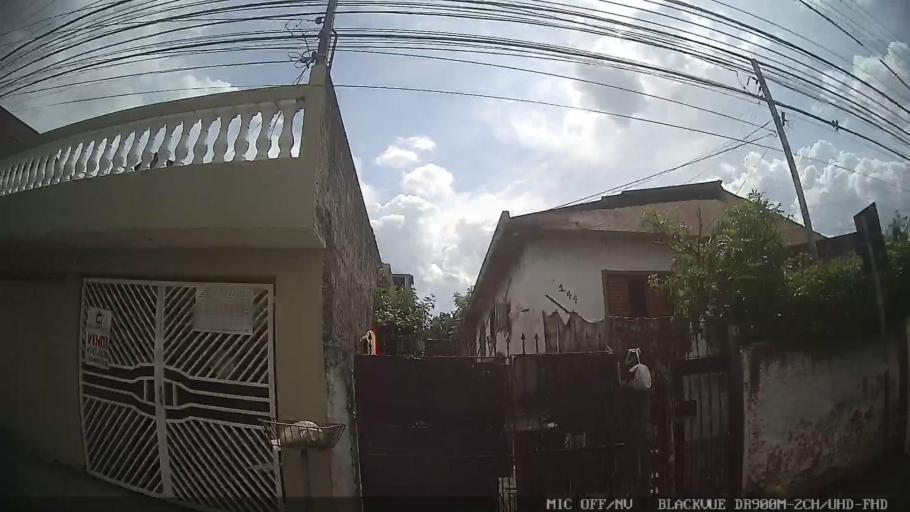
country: BR
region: Sao Paulo
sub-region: Poa
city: Poa
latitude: -23.5258
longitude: -46.3406
